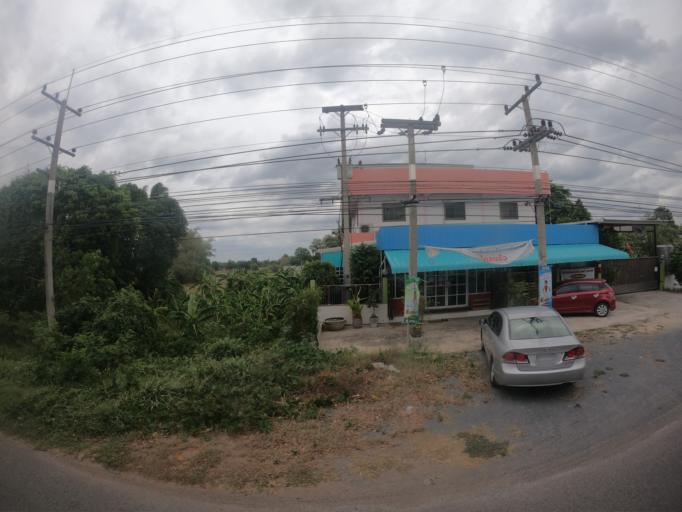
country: TH
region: Nakhon Ratchasima
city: Chok Chai
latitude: 14.7672
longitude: 102.1627
